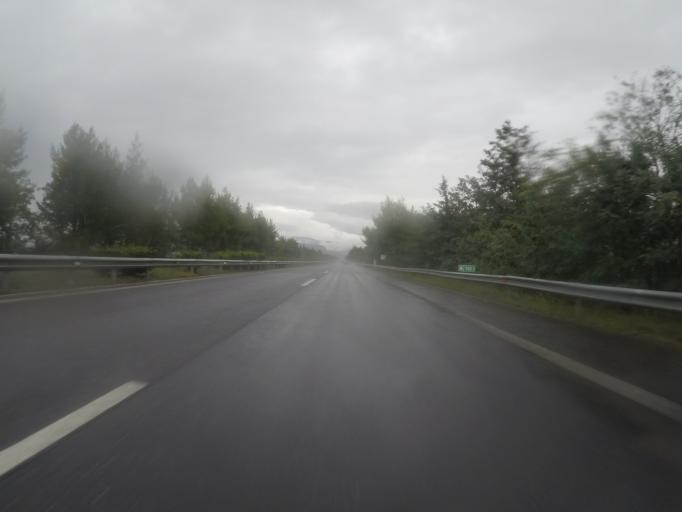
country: GR
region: Peloponnese
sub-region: Nomos Arkadias
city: Tripoli
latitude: 37.5480
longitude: 22.4186
